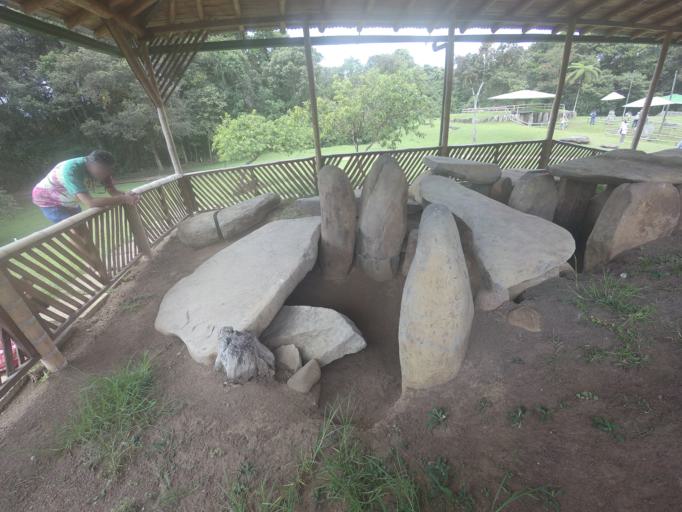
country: CO
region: Huila
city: San Agustin
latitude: 1.8839
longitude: -76.2960
